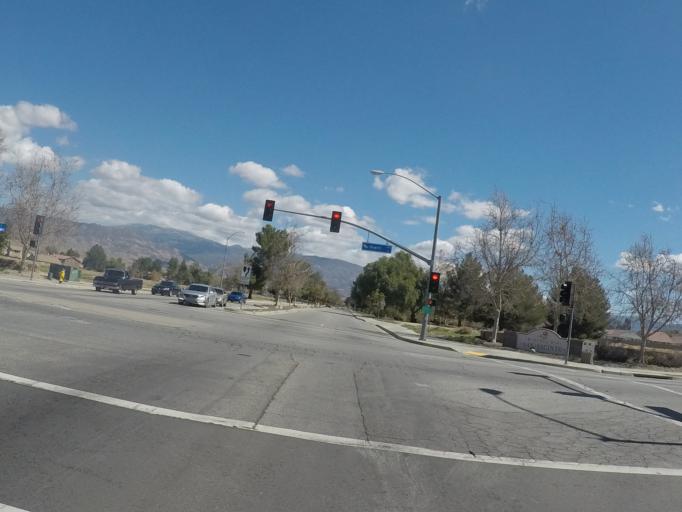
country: US
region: California
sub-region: Riverside County
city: San Jacinto
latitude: 33.7722
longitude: -116.9512
